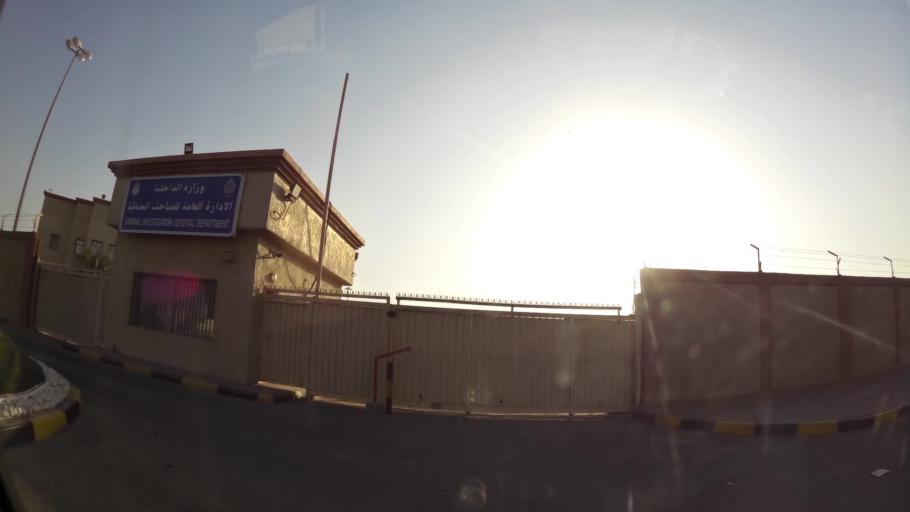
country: KW
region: Muhafazat Hawalli
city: As Salimiyah
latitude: 29.3273
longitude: 48.0763
